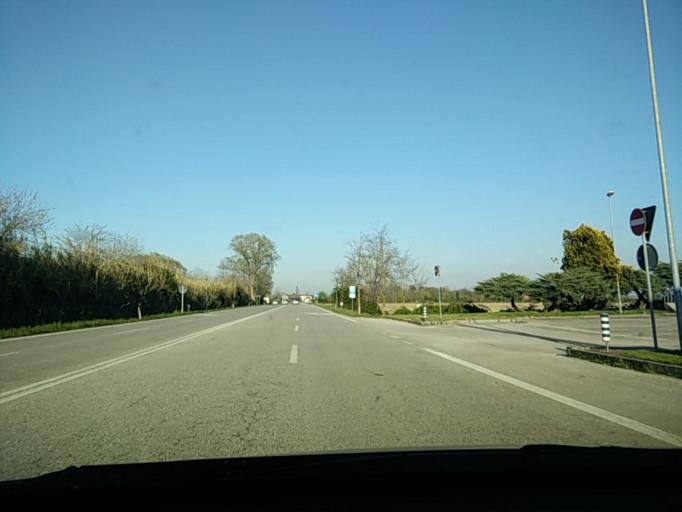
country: IT
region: Veneto
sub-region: Provincia di Venezia
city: San Liberale
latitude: 45.5270
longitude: 12.3793
